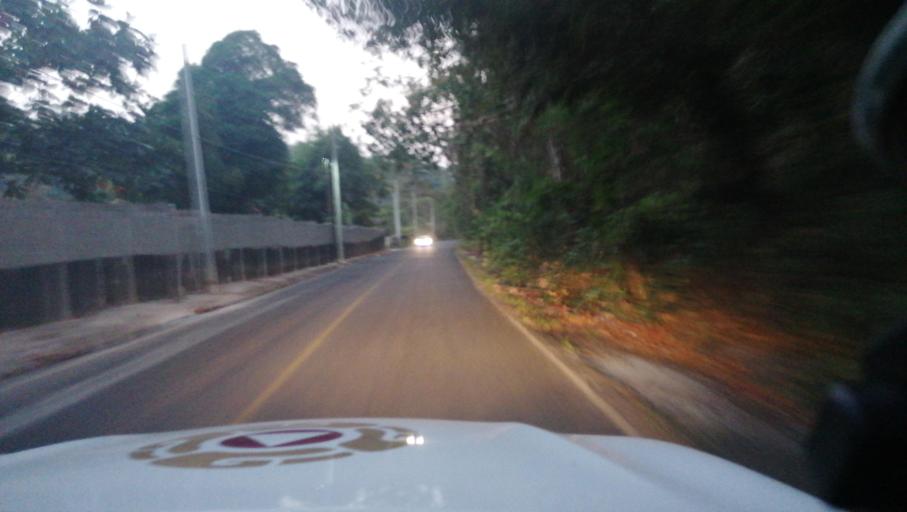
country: MX
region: Chiapas
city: Veinte de Noviembre
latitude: 14.9964
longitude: -92.2430
